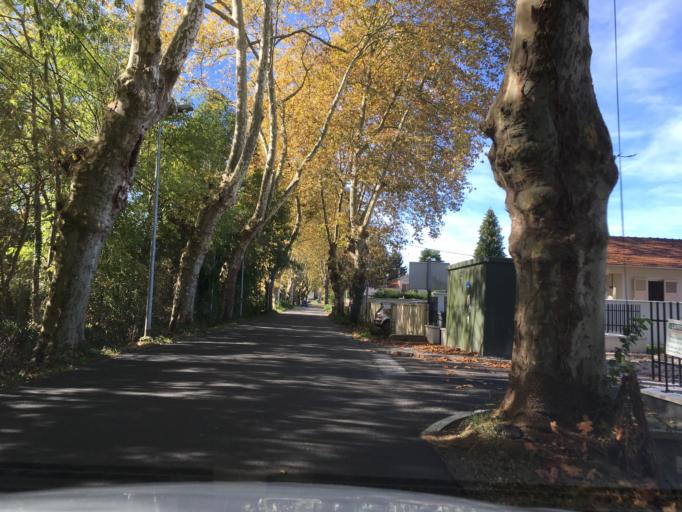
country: FR
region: Aquitaine
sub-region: Departement des Pyrenees-Atlantiques
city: Pau
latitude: 43.3277
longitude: -0.3458
